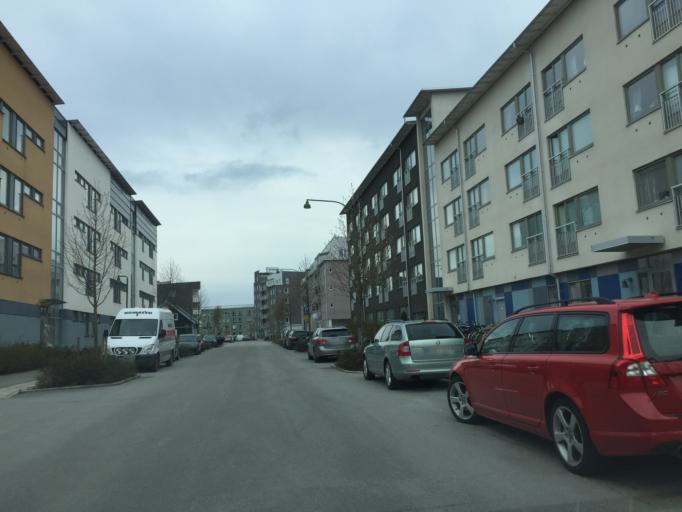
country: SE
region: OErebro
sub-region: Orebro Kommun
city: Orebro
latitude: 59.2574
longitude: 15.2219
